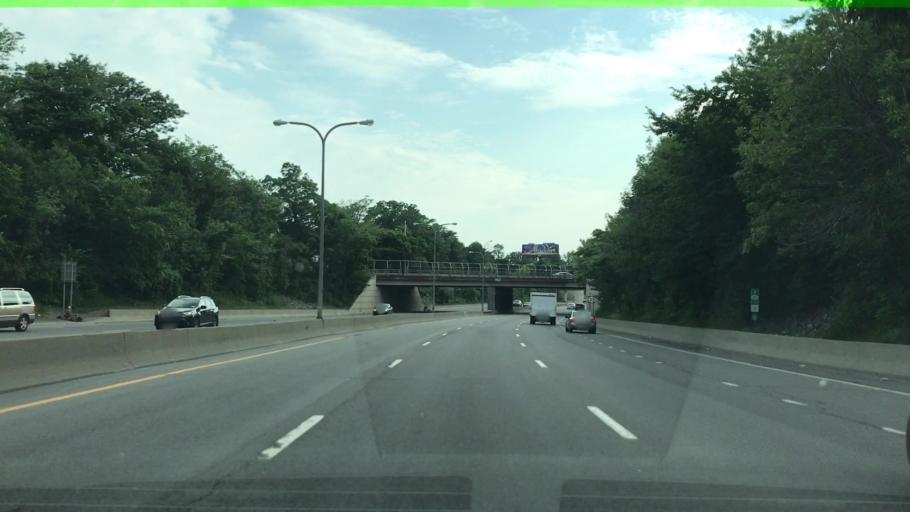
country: US
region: New York
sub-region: Erie County
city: Buffalo
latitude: 42.9012
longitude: -78.8476
